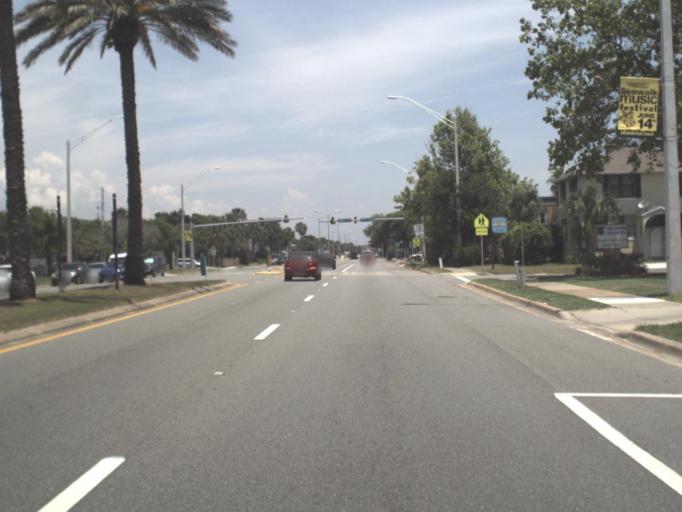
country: US
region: Florida
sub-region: Duval County
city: Neptune Beach
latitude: 30.3063
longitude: -81.3954
